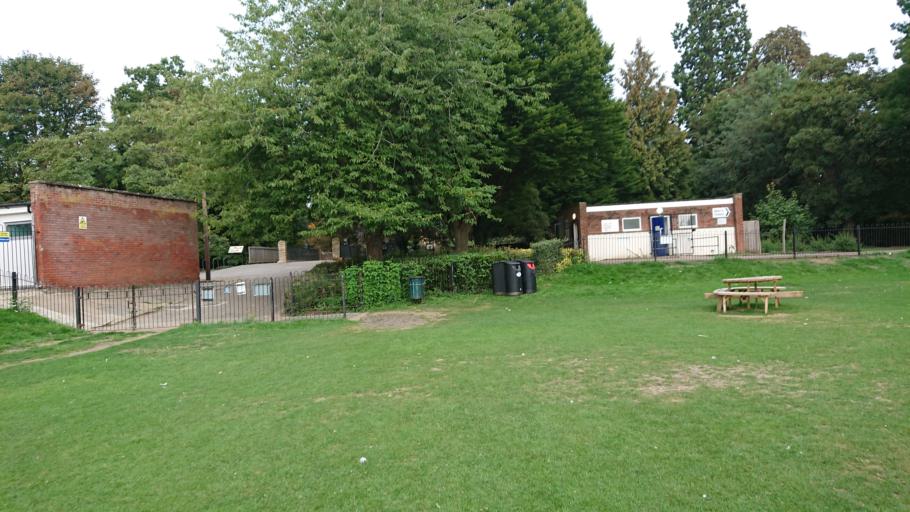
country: GB
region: England
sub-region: Oxfordshire
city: Abingdon
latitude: 51.6701
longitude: -1.2762
